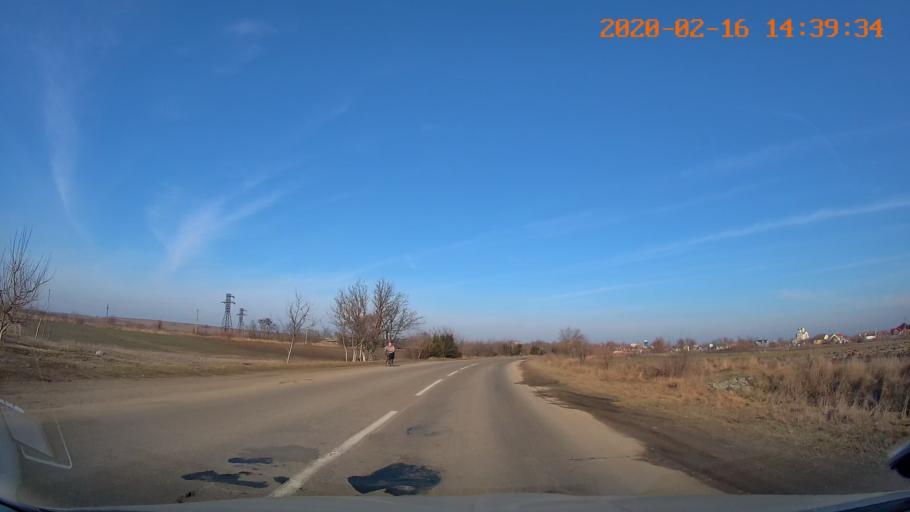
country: RO
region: Botosani
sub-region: Comuna Darabani
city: Bajura
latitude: 48.2446
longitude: 26.5502
